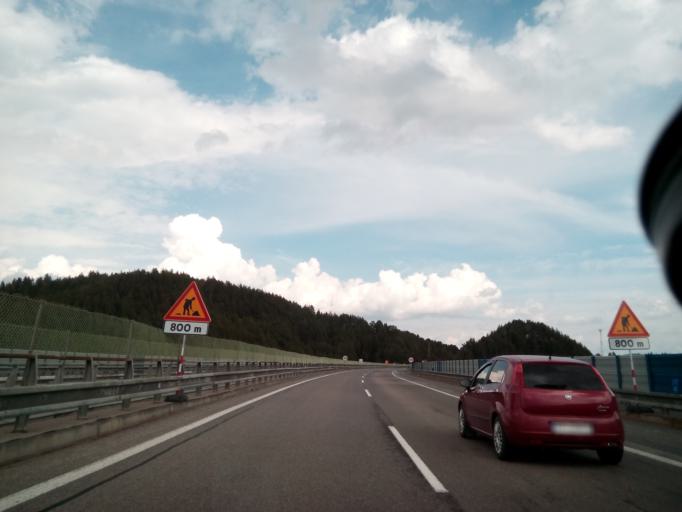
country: SK
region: Zilinsky
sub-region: Okres Zilina
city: Liptovsky Hradok
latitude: 49.0574
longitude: 19.6933
